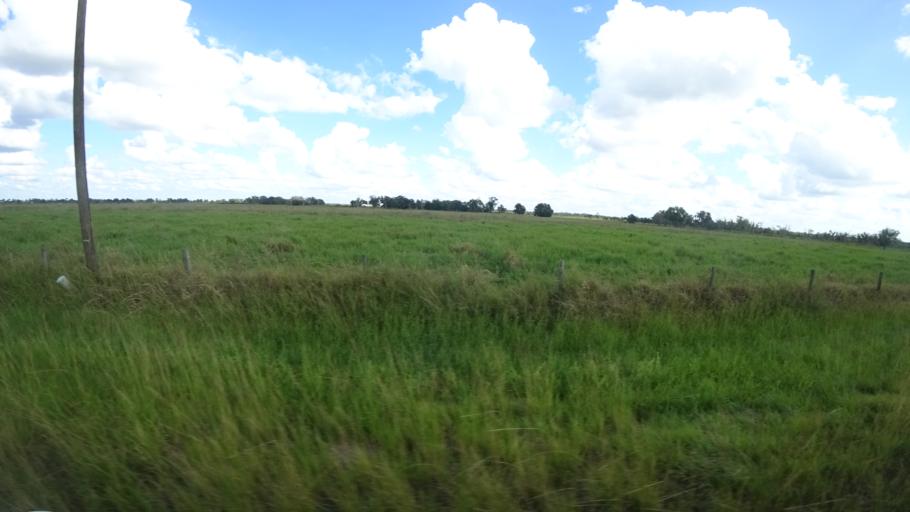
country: US
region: Florida
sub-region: DeSoto County
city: Nocatee
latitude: 27.2855
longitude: -82.1134
